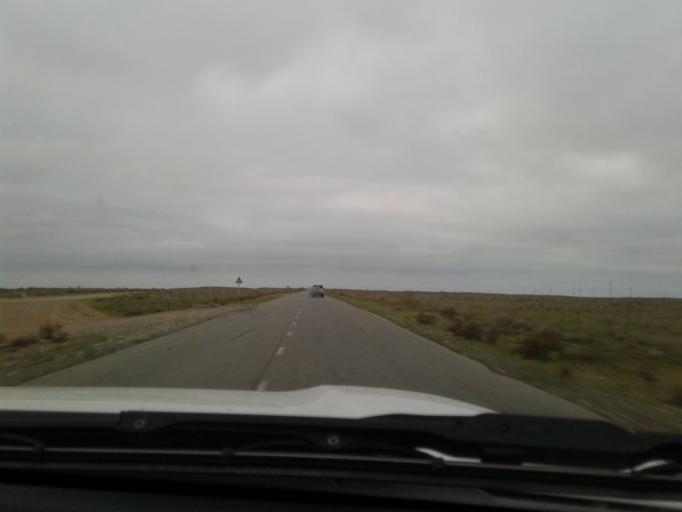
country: TM
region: Lebap
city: Turkmenabat
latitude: 39.0558
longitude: 63.7497
